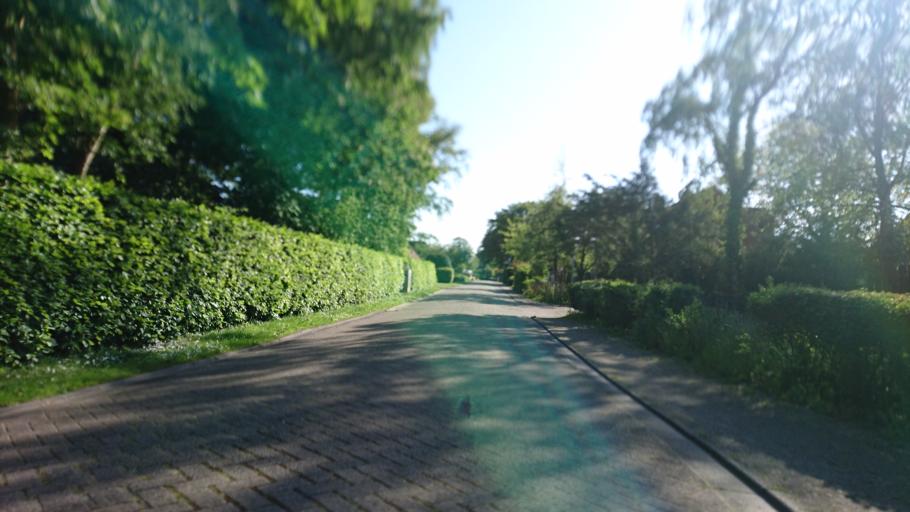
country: DE
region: Lower Saxony
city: Norden
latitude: 53.5867
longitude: 7.2162
